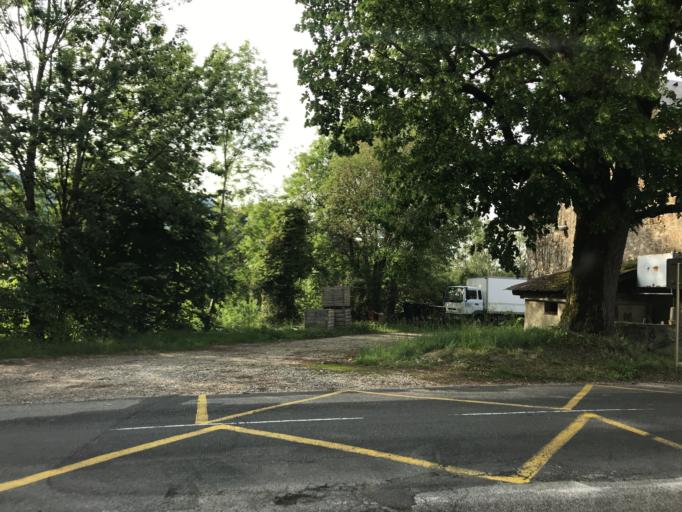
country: FR
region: Rhone-Alpes
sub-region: Departement de la Savoie
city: Vimines
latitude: 45.5614
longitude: 5.8557
